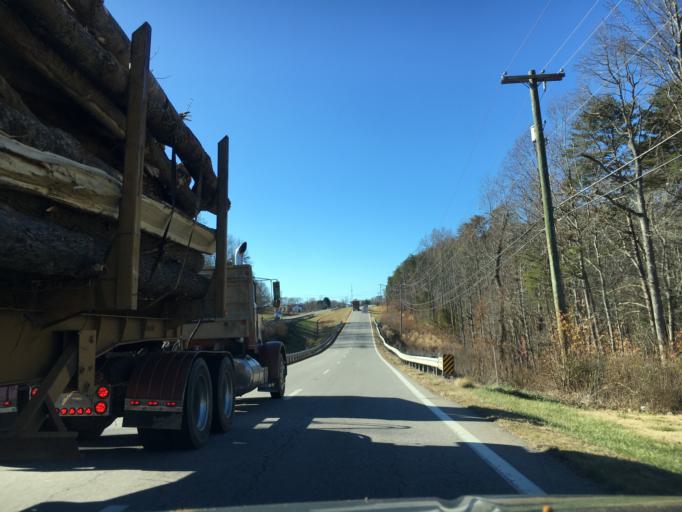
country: US
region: Virginia
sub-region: Henry County
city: Chatmoss
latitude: 36.6238
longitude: -79.6171
